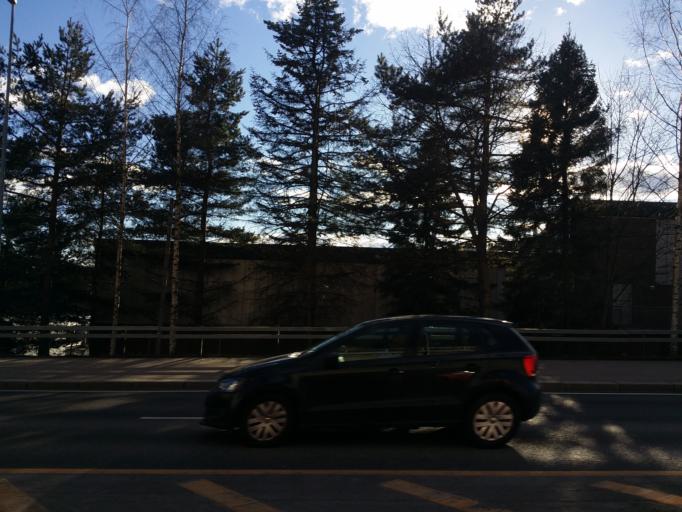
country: NO
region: Oslo
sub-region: Oslo
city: Oslo
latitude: 59.8828
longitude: 10.7707
